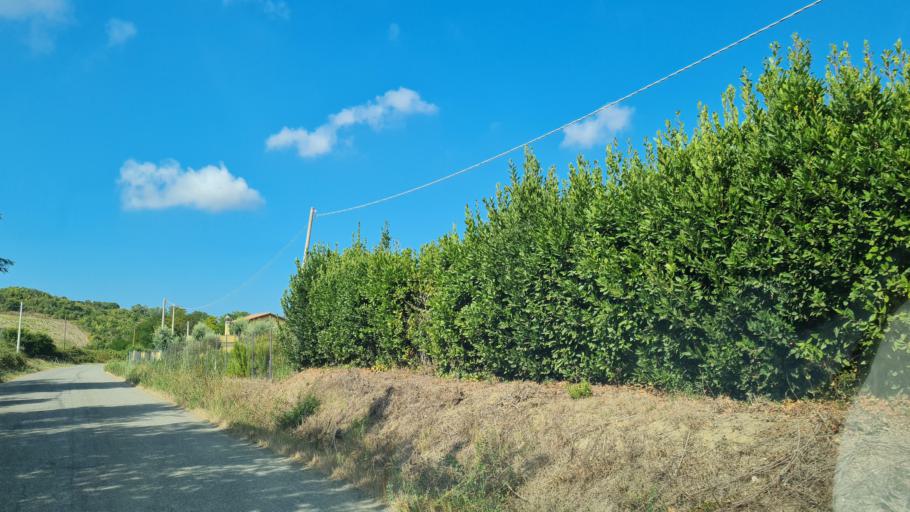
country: IT
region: Latium
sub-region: Provincia di Viterbo
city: Tarquinia
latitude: 42.2601
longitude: 11.7536
